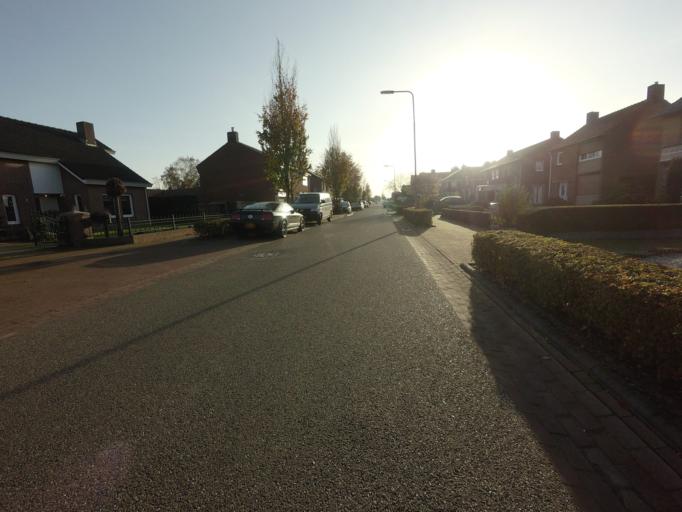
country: DE
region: North Rhine-Westphalia
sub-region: Regierungsbezirk Koln
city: Waldfeucht
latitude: 51.0824
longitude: 5.9656
